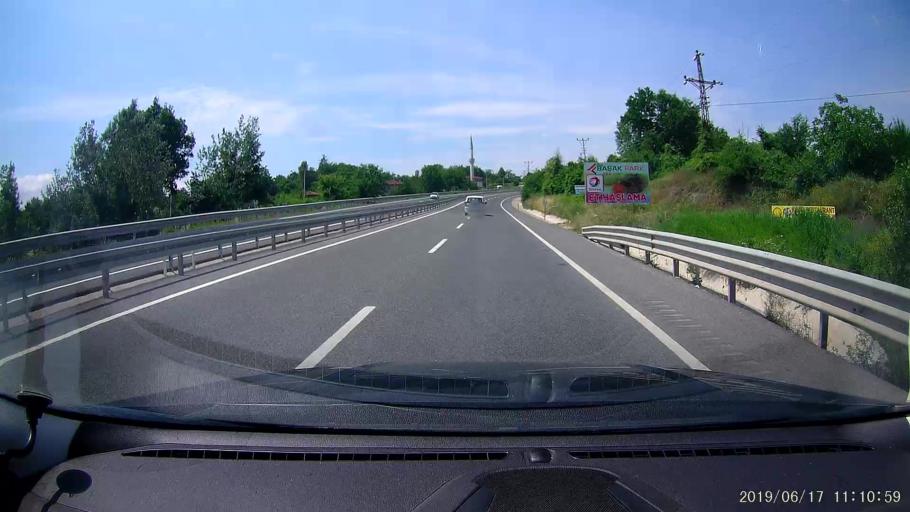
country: TR
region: Kastamonu
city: Tosya
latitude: 40.9926
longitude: 34.0157
